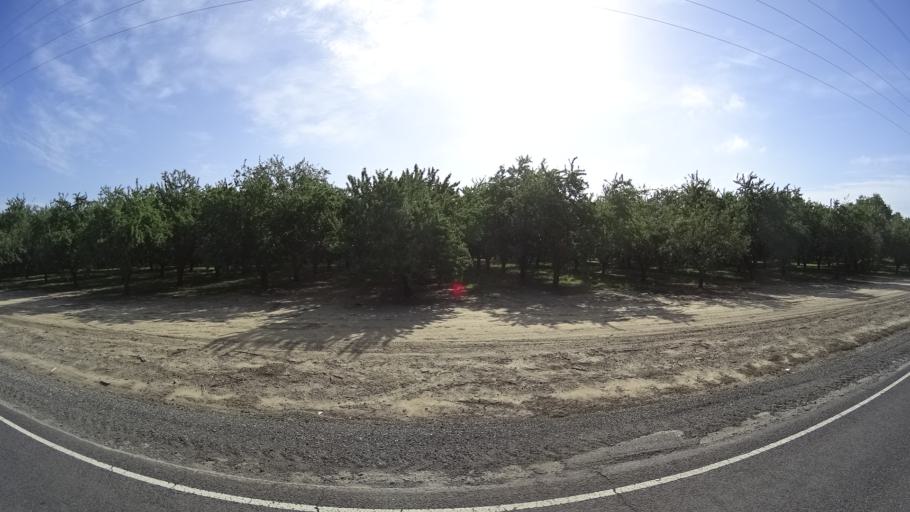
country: US
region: California
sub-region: Glenn County
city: Hamilton City
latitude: 39.6146
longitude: -122.0074
